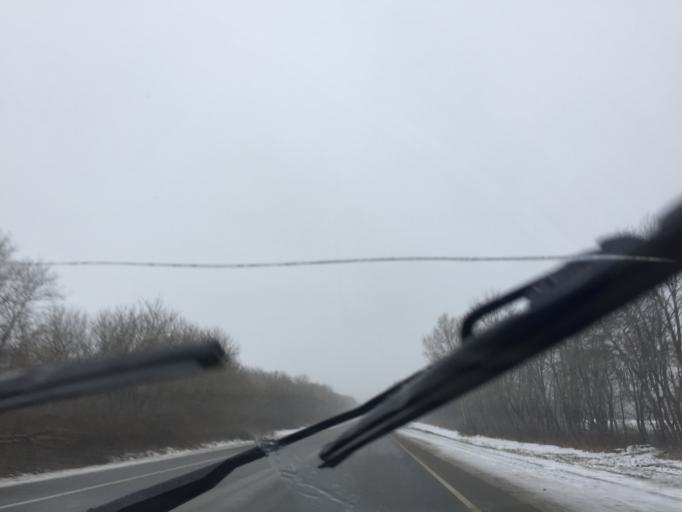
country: RU
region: Tula
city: Plavsk
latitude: 53.7661
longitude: 37.3437
